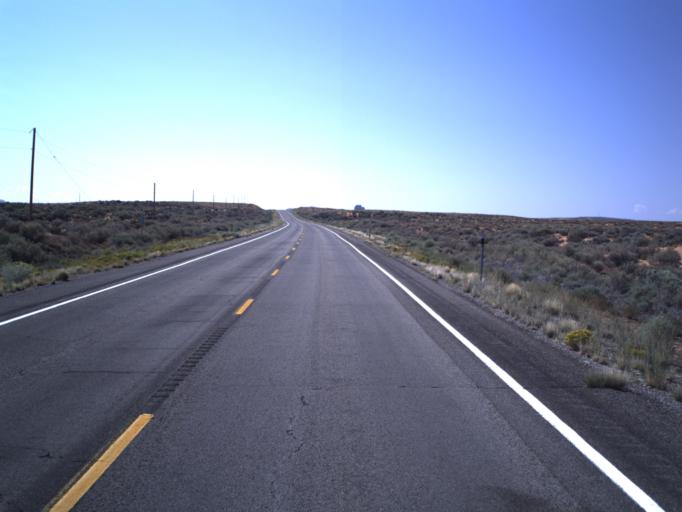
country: US
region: Utah
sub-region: San Juan County
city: Blanding
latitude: 37.0963
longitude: -109.5477
